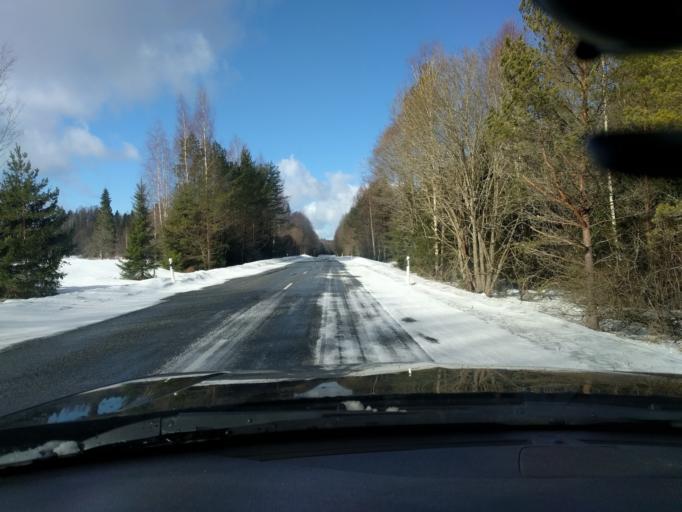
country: EE
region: Harju
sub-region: Anija vald
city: Kehra
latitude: 59.2131
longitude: 25.5004
